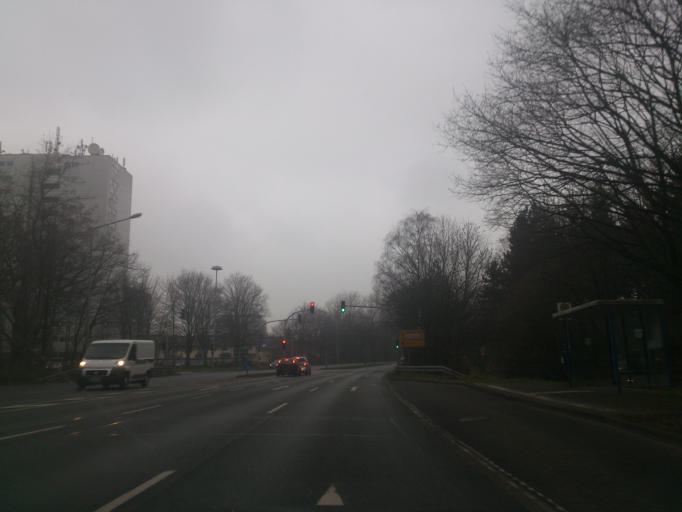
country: DE
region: North Rhine-Westphalia
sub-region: Regierungsbezirk Detmold
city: Paderborn
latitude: 51.7099
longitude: 8.7806
